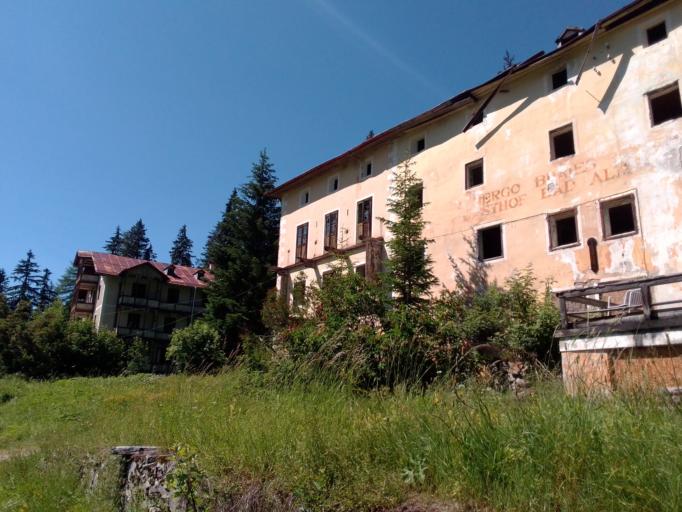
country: IT
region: Trentino-Alto Adige
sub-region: Bolzano
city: Braies
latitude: 46.7070
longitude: 12.1553
